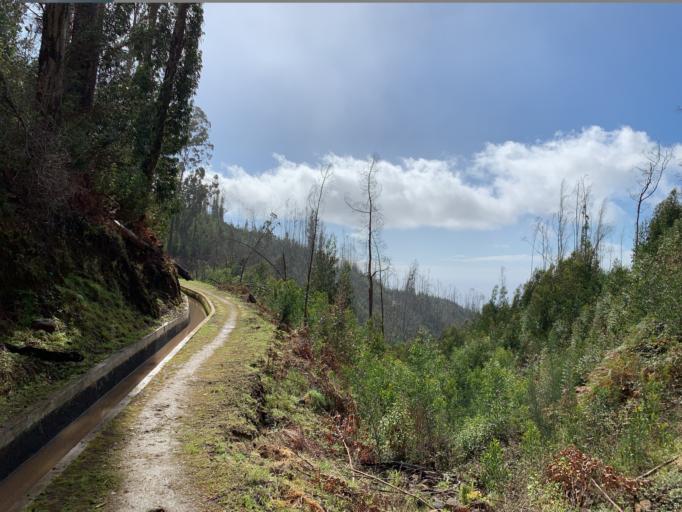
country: PT
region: Madeira
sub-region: Calheta
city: Estreito da Calheta
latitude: 32.7468
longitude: -17.1636
